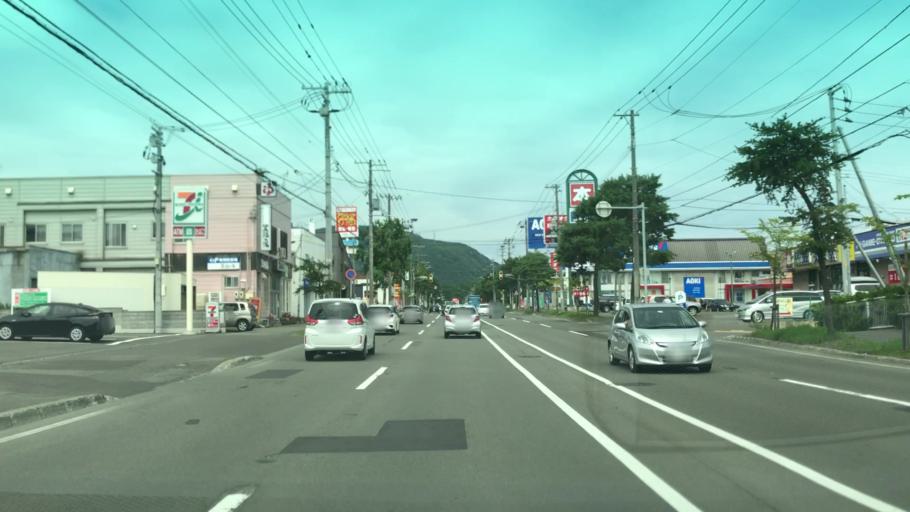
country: JP
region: Hokkaido
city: Sapporo
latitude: 43.0742
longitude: 141.2784
